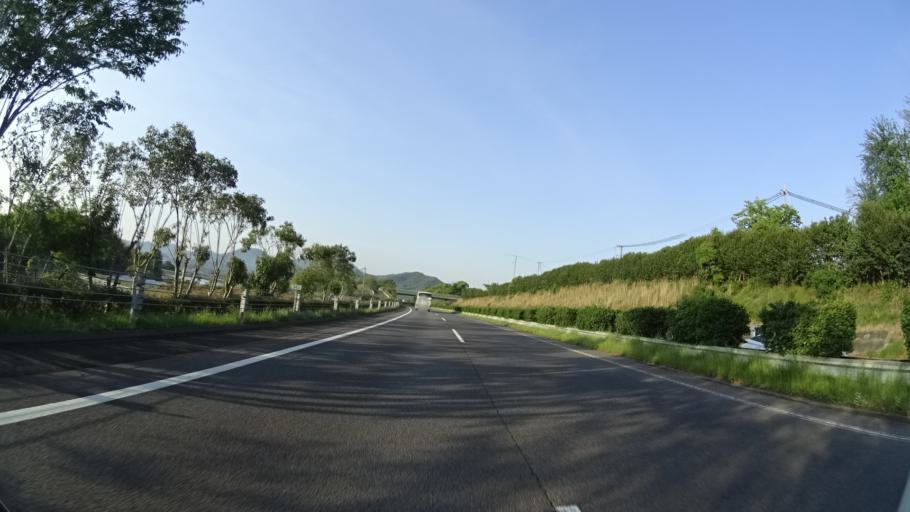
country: JP
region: Kagawa
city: Kan'onjicho
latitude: 34.1605
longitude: 133.7282
